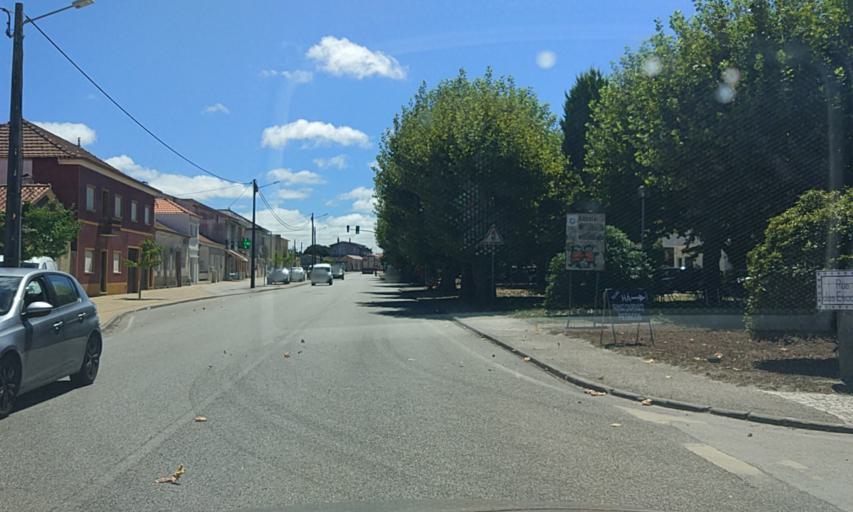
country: PT
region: Coimbra
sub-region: Mira
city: Mira
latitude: 40.4426
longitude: -8.7272
